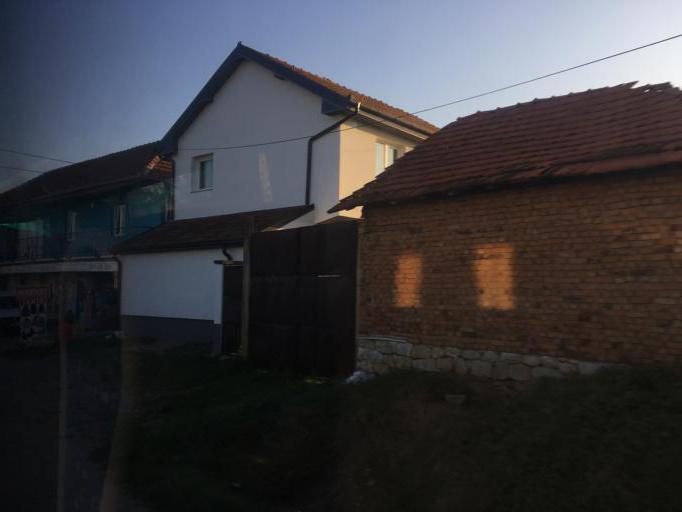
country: XK
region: Pristina
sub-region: Komuna e Drenasit
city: Glogovac
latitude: 42.5933
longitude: 20.8921
